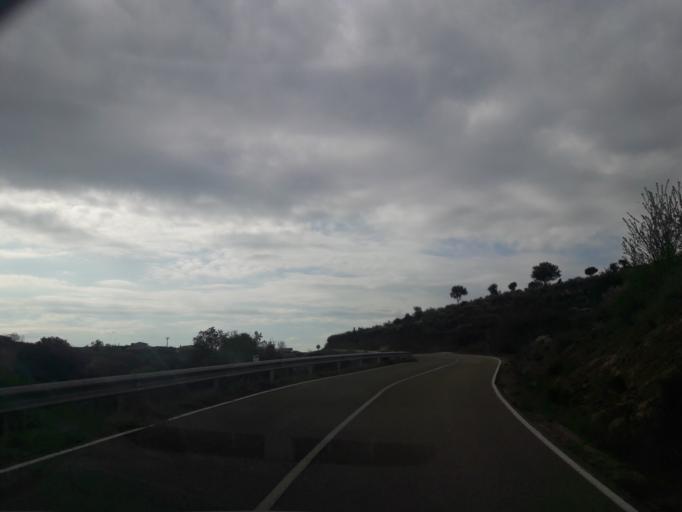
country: ES
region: Castille and Leon
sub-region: Provincia de Salamanca
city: Pastores
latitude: 40.5171
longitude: -6.5144
